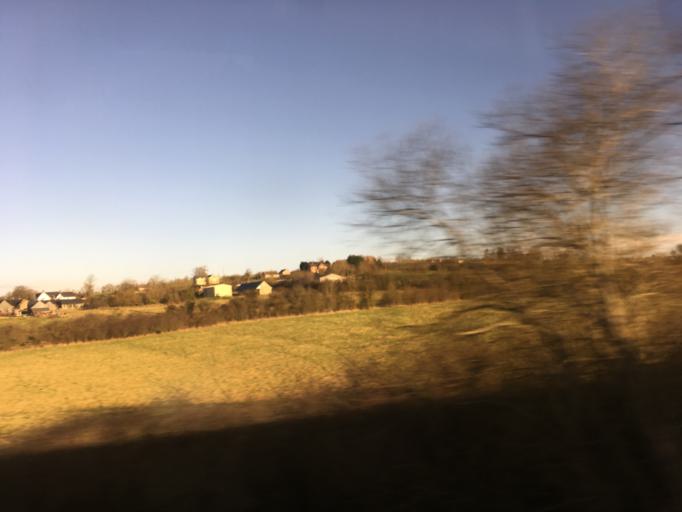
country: GB
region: England
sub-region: Wiltshire
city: Lyneham
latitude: 51.5576
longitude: -1.9744
